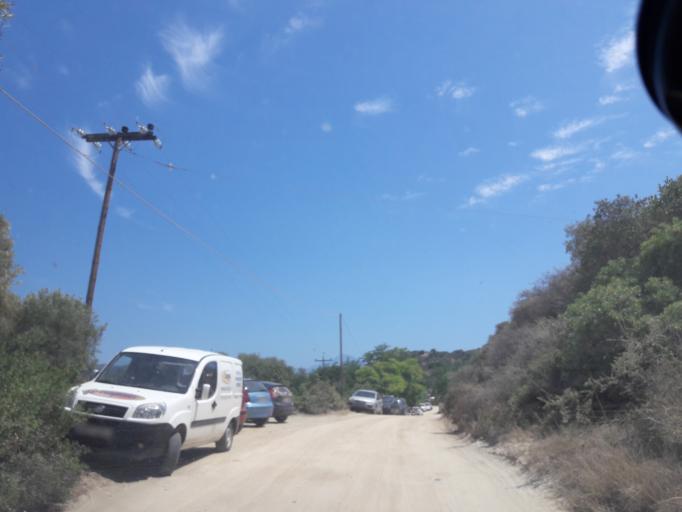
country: GR
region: Central Macedonia
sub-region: Nomos Chalkidikis
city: Ouranoupolis
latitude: 40.3162
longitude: 23.9371
